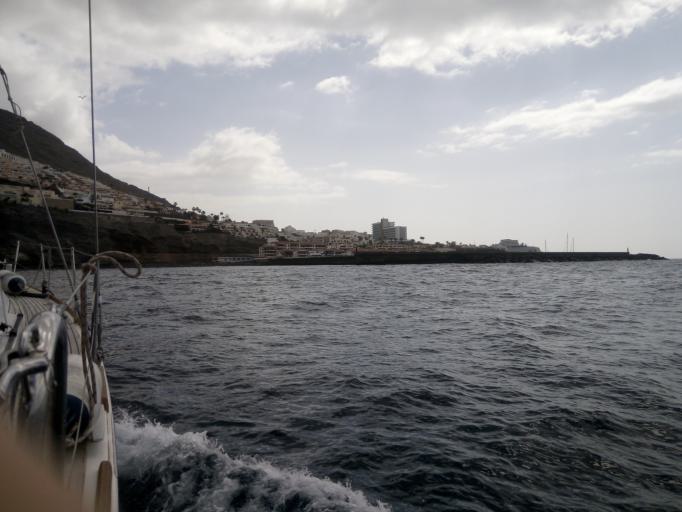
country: ES
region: Canary Islands
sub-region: Provincia de Santa Cruz de Tenerife
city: Santiago del Teide
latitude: 28.2515
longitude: -16.8421
